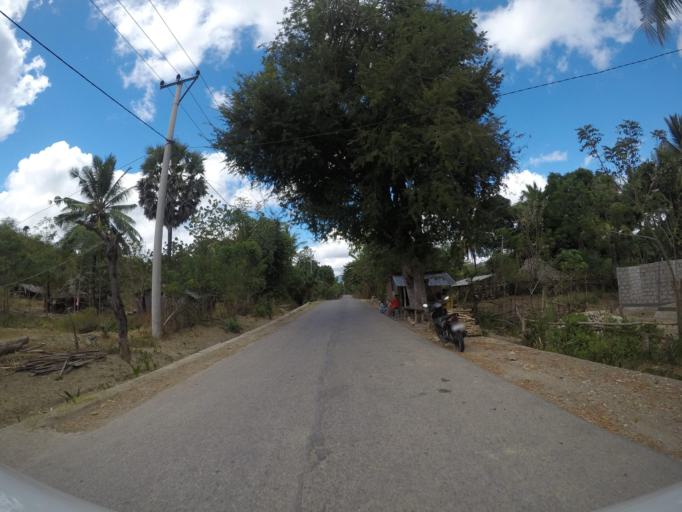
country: TL
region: Lautem
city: Lospalos
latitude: -8.4474
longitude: 126.8241
